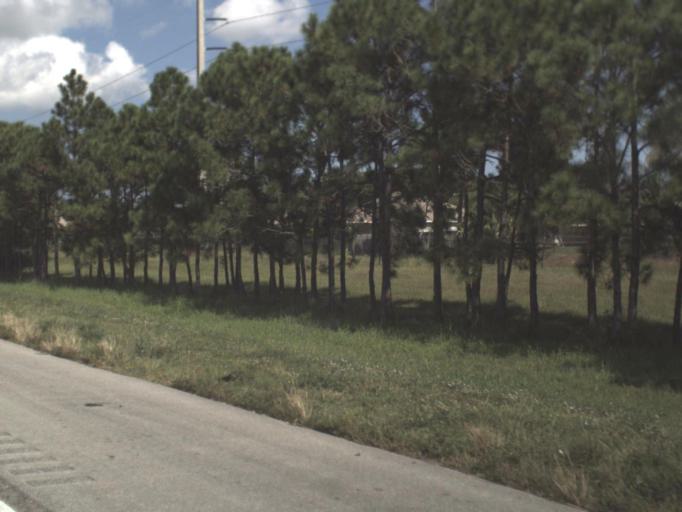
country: US
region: Florida
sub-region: Saint Lucie County
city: River Park
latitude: 27.3414
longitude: -80.3742
